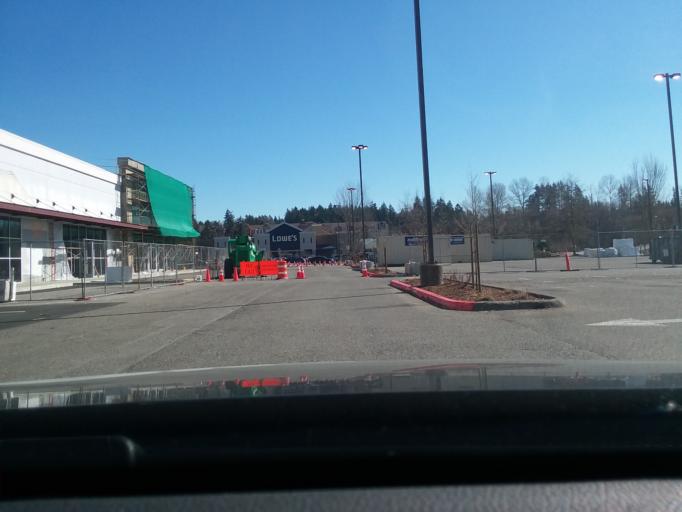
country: US
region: Washington
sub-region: Pierce County
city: South Hill
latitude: 47.1572
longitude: -122.2894
